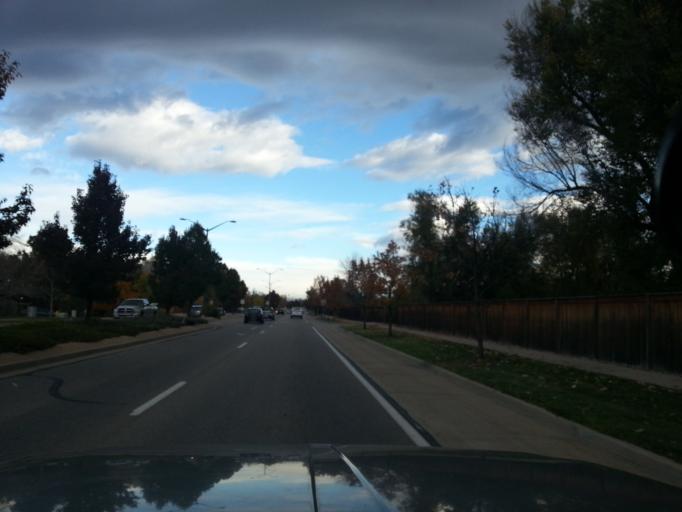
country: US
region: Colorado
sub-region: Larimer County
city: Fort Collins
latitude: 40.5455
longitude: -105.1151
